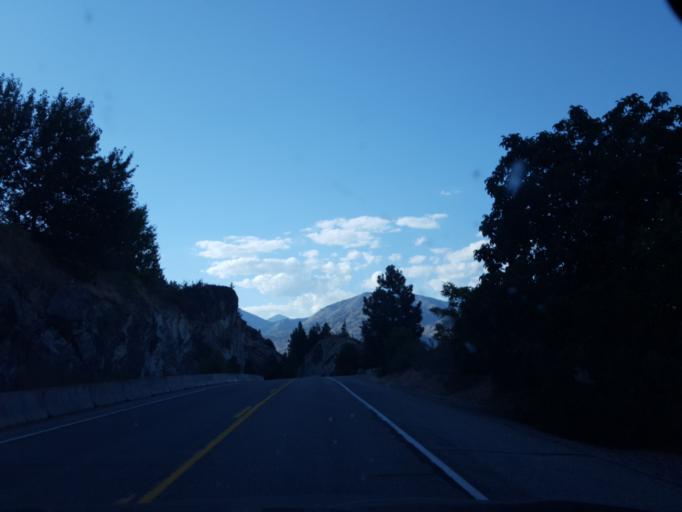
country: US
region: Washington
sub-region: Chelan County
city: Granite Falls
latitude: 47.9623
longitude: -120.2106
